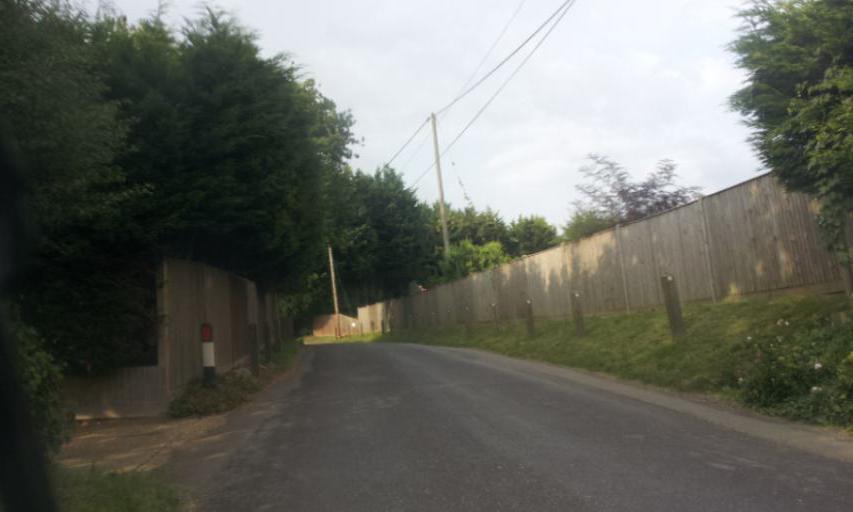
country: GB
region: England
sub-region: Kent
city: Yalding
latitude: 51.2355
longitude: 0.4238
